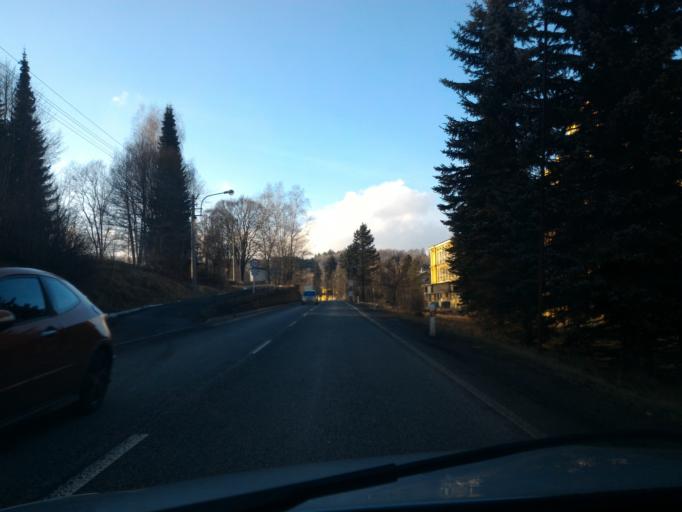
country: CZ
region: Liberecky
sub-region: Okres Jablonec nad Nisou
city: Tanvald
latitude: 50.7346
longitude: 15.2923
